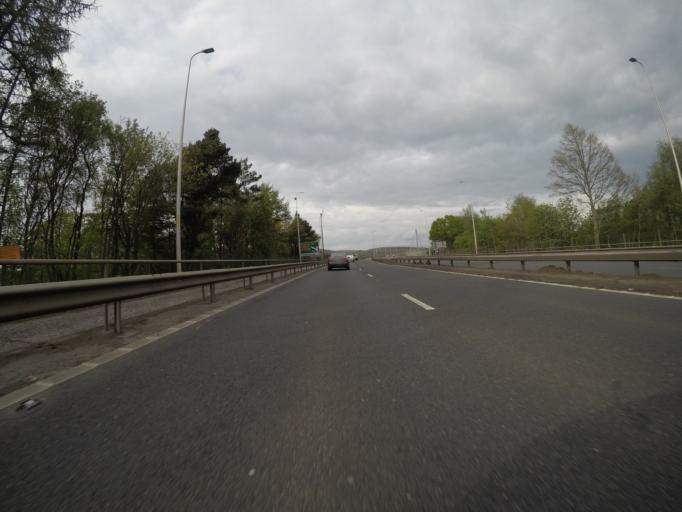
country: GB
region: Scotland
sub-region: West Dunbartonshire
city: Old Kilpatrick
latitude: 55.9167
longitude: -4.4702
